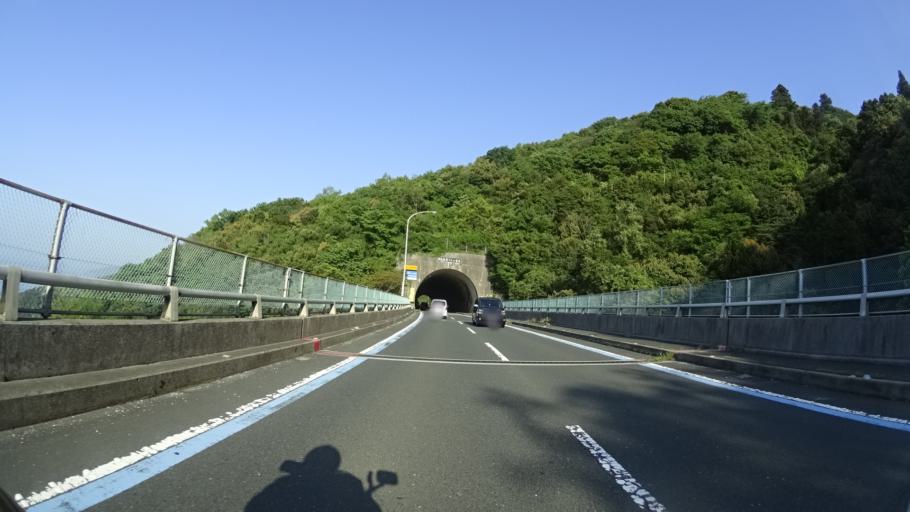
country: JP
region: Ehime
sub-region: Nishiuwa-gun
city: Ikata-cho
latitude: 33.4318
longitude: 132.2221
